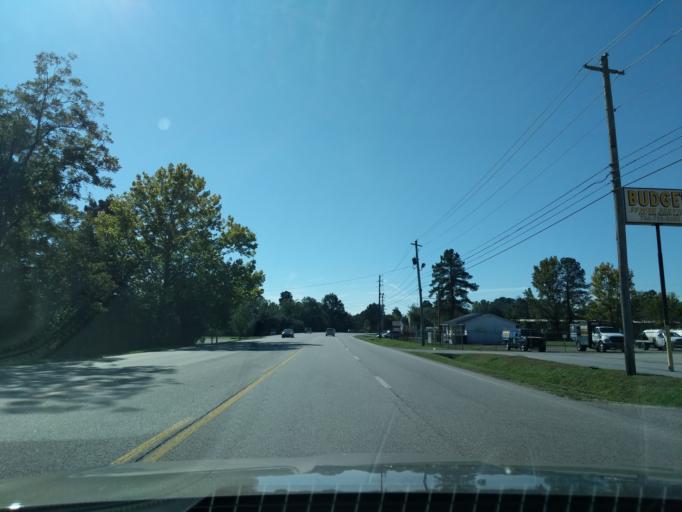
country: US
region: Georgia
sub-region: Richmond County
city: Augusta
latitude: 33.4257
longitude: -82.0062
